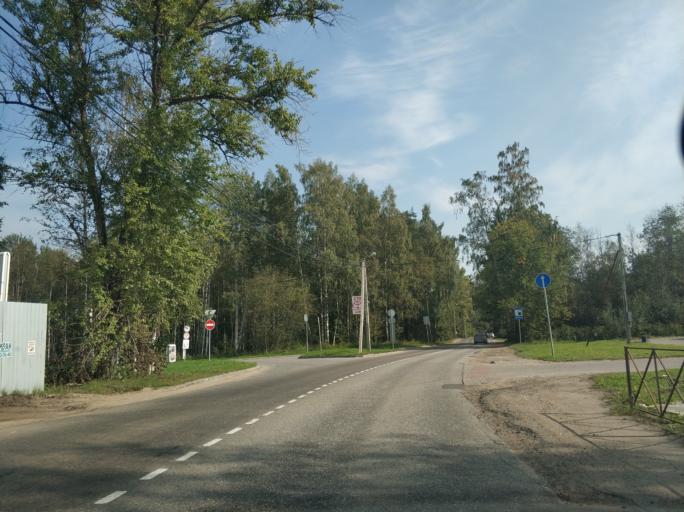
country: RU
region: Leningrad
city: Yanino Vtoroye
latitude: 60.0129
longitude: 30.5869
